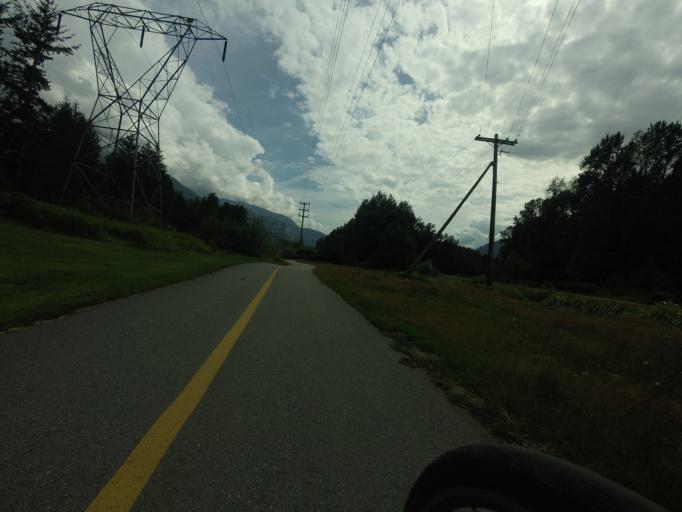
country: CA
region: British Columbia
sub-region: Greater Vancouver Regional District
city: Lions Bay
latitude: 49.7325
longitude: -123.1349
